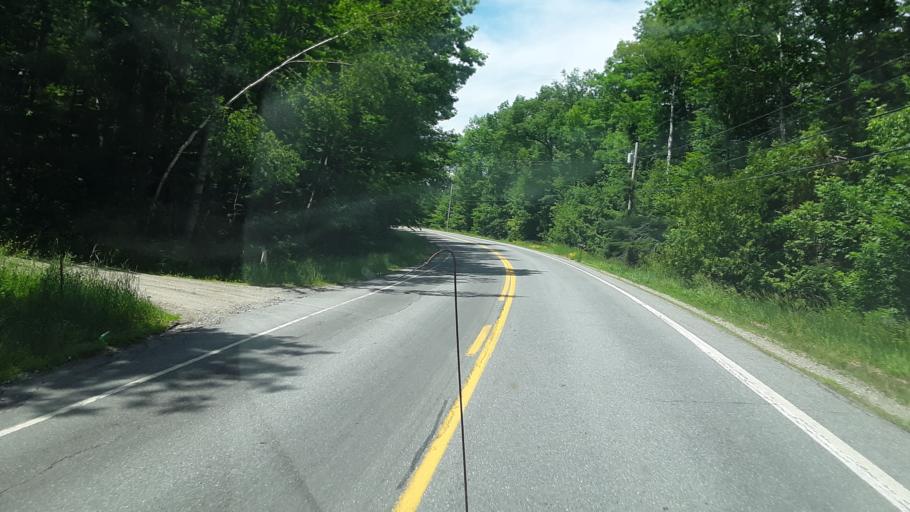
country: US
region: Maine
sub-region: Hancock County
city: Bucksport
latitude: 44.5711
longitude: -68.8193
